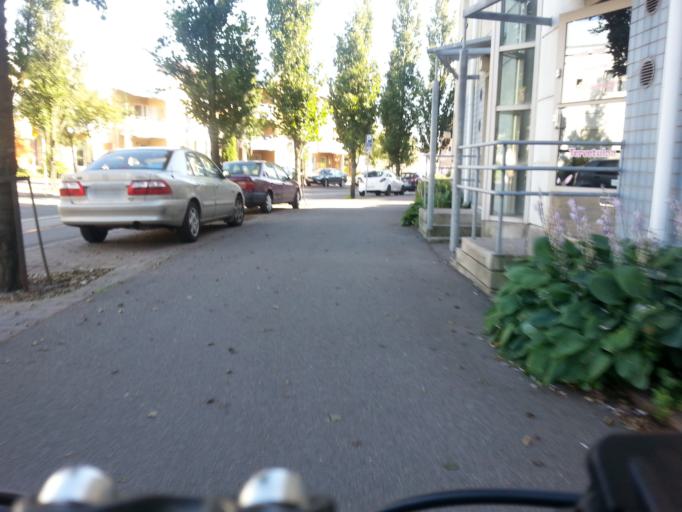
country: FI
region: Uusimaa
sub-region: Helsinki
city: Helsinki
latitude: 60.2063
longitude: 24.8917
